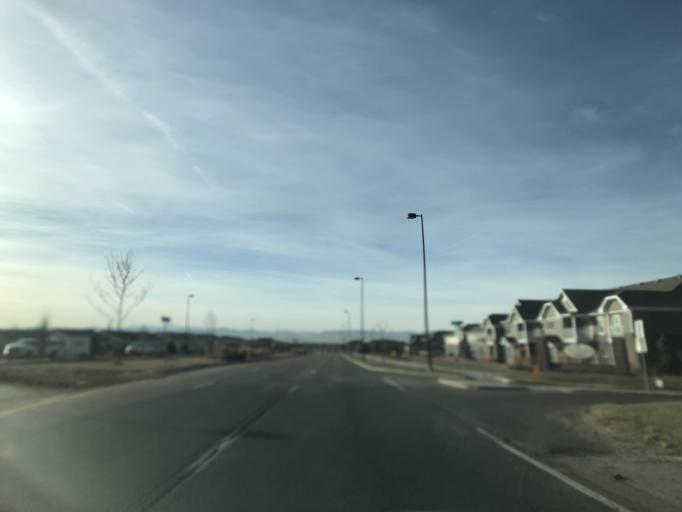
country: US
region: Colorado
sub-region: Adams County
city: Aurora
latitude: 39.7985
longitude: -104.7577
